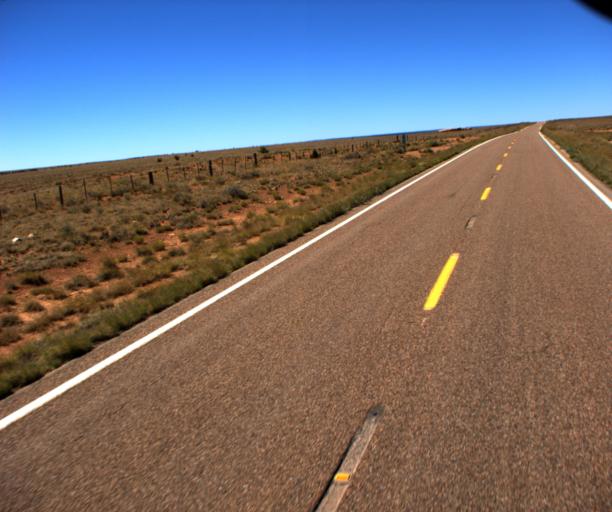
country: US
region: Arizona
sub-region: Navajo County
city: Winslow
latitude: 34.8696
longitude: -110.6571
